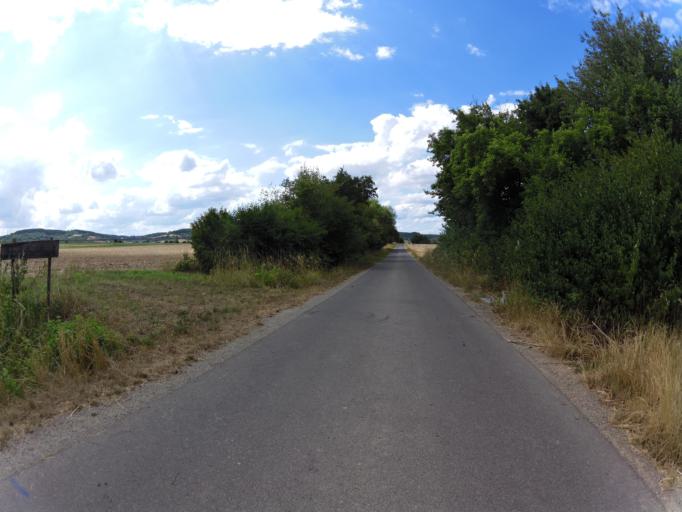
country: DE
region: Bavaria
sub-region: Regierungsbezirk Unterfranken
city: Zellingen
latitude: 49.8838
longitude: 9.8166
